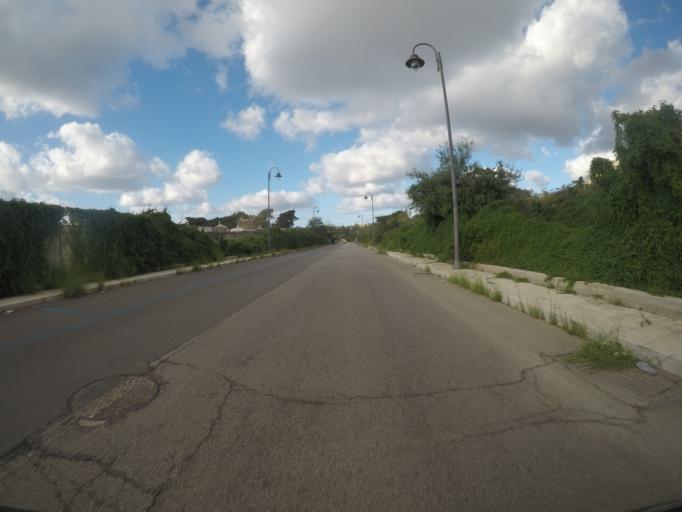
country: IT
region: Sicily
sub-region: Palermo
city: Isola delle Femmine
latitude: 38.1910
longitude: 13.2454
